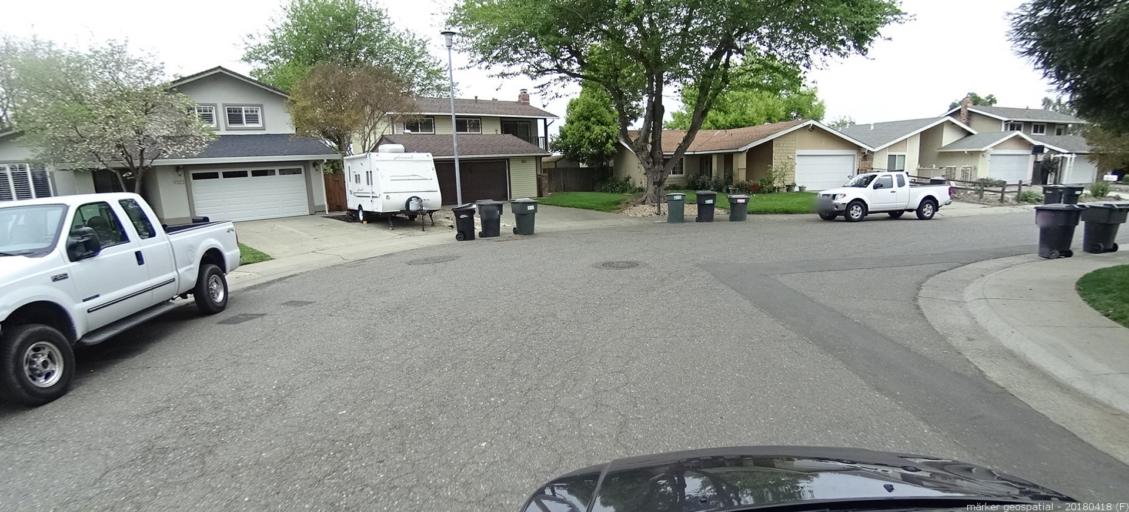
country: US
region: California
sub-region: Sacramento County
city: La Riviera
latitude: 38.5709
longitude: -121.3528
